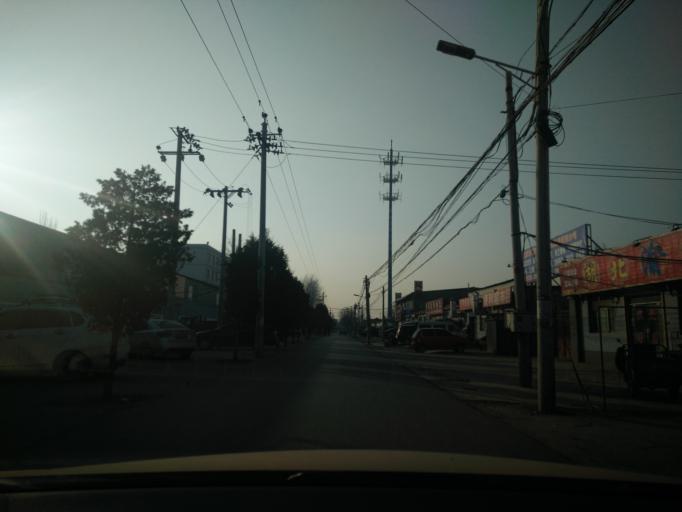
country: CN
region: Beijing
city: Yinghai
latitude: 39.7176
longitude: 116.4316
